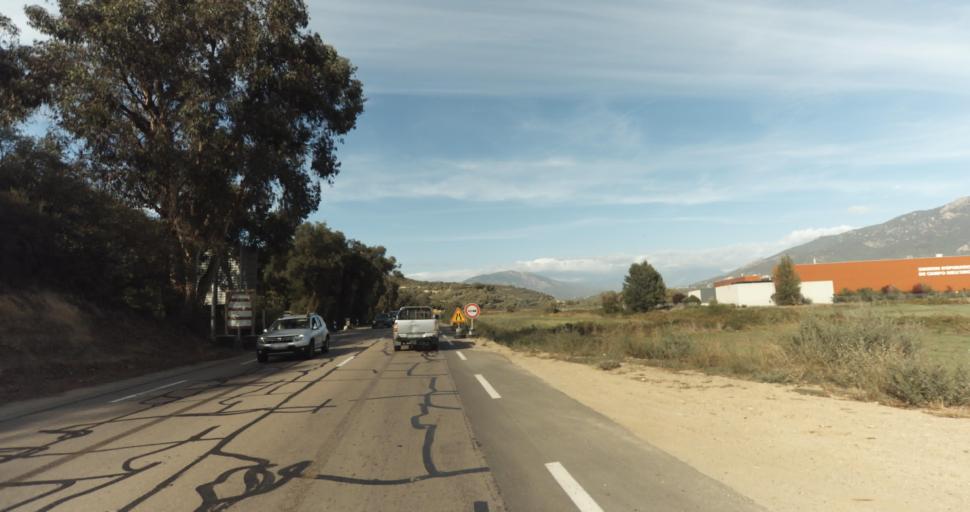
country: FR
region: Corsica
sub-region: Departement de la Corse-du-Sud
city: Afa
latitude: 41.9346
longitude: 8.8028
